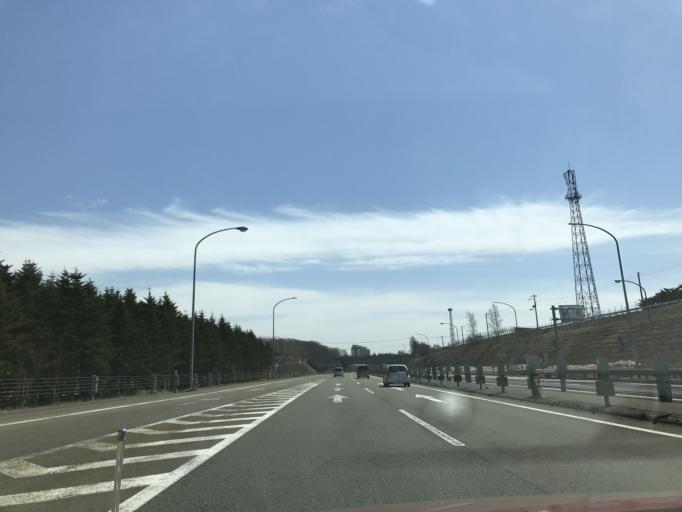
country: JP
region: Hokkaido
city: Ebetsu
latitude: 43.0933
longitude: 141.4988
